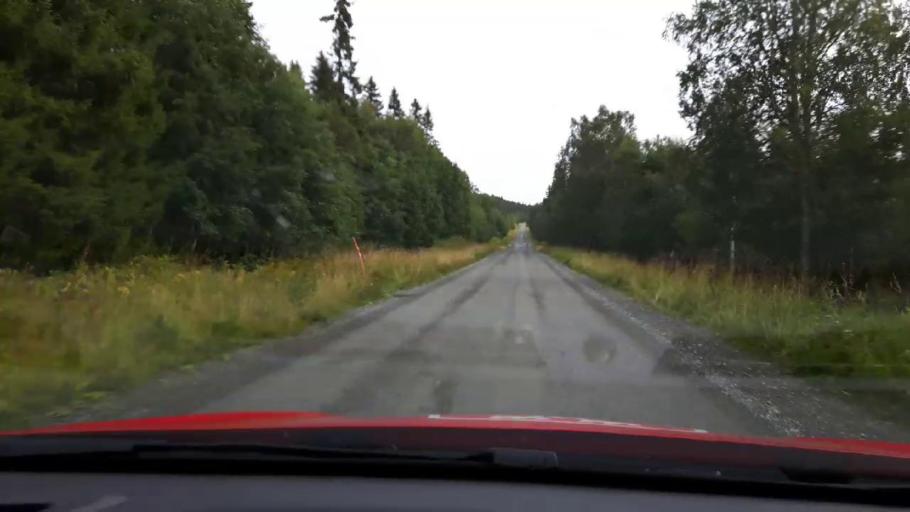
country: SE
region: Jaemtland
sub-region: Are Kommun
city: Are
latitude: 63.7445
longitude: 12.9808
